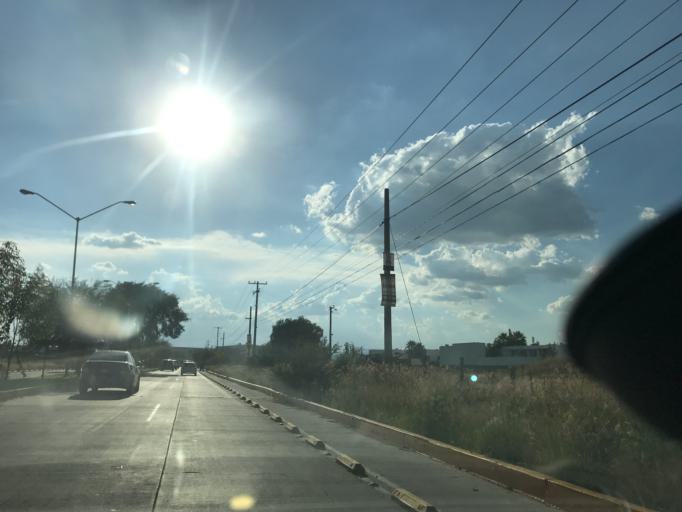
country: MX
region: Aguascalientes
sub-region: Aguascalientes
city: Pocitos
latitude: 21.9099
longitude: -102.3263
